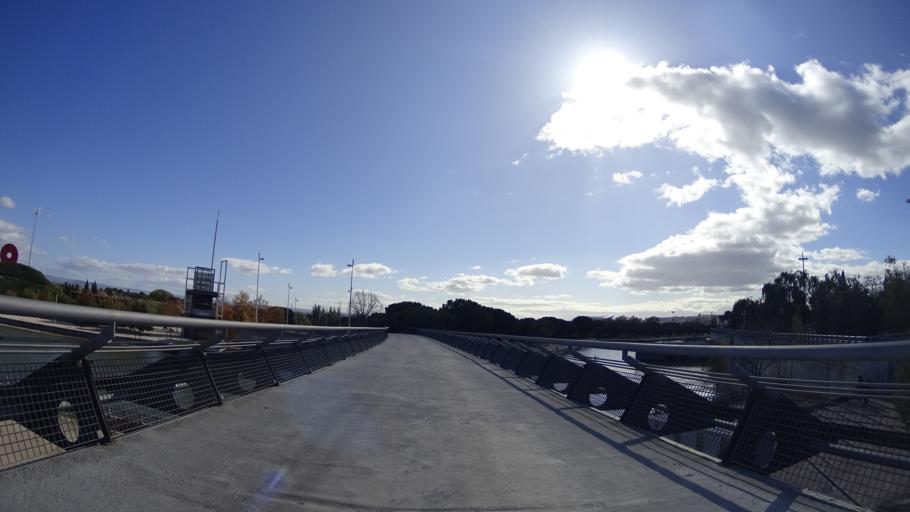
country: ES
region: Madrid
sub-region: Provincia de Madrid
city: San Blas
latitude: 40.4589
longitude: -3.6087
